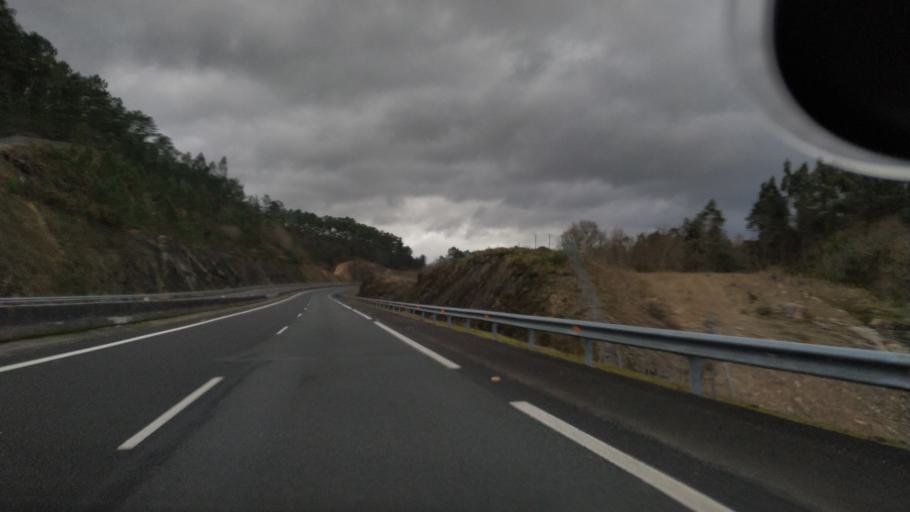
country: ES
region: Galicia
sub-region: Provincia da Coruna
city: Vedra
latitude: 42.7939
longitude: -8.4815
